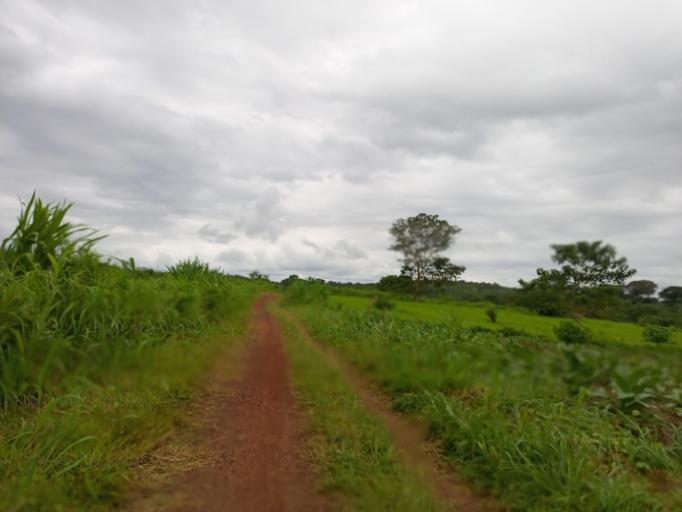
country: SL
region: Northern Province
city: Kamakwie
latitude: 9.5054
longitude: -12.2640
